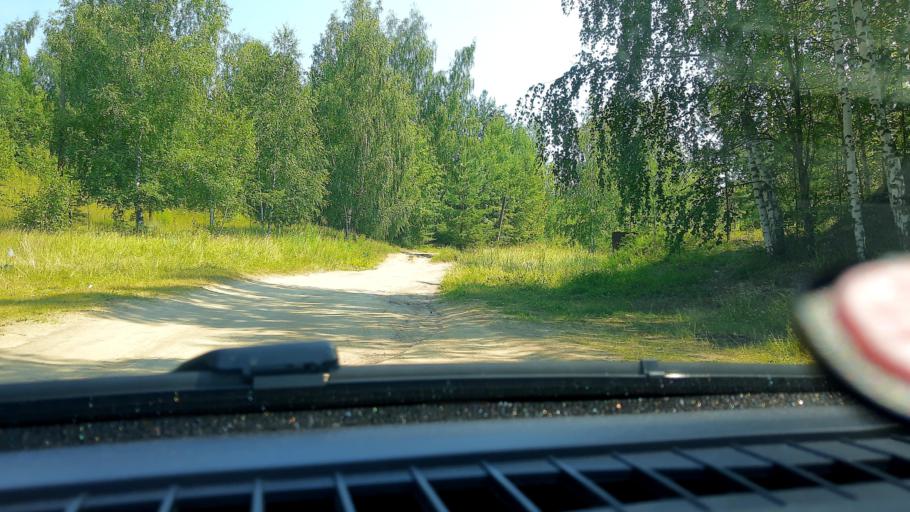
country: RU
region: Nizjnij Novgorod
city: Zavolzh'ye
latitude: 56.6885
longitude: 43.4258
